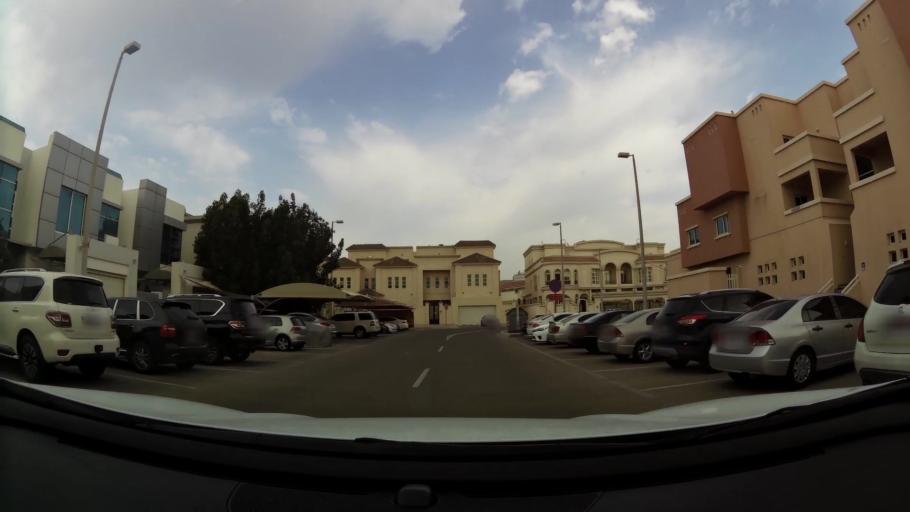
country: AE
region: Abu Dhabi
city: Abu Dhabi
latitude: 24.4750
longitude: 54.3850
